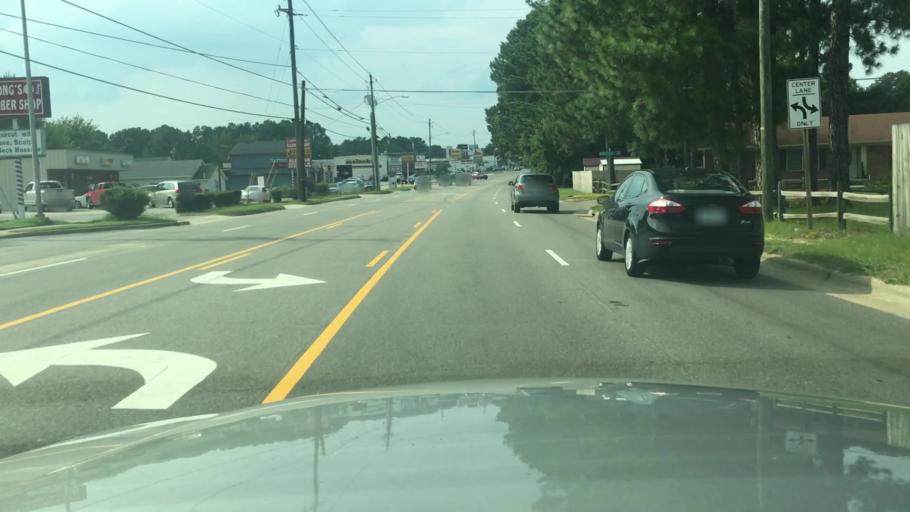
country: US
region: North Carolina
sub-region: Cumberland County
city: Fort Bragg
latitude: 35.0946
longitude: -78.9867
